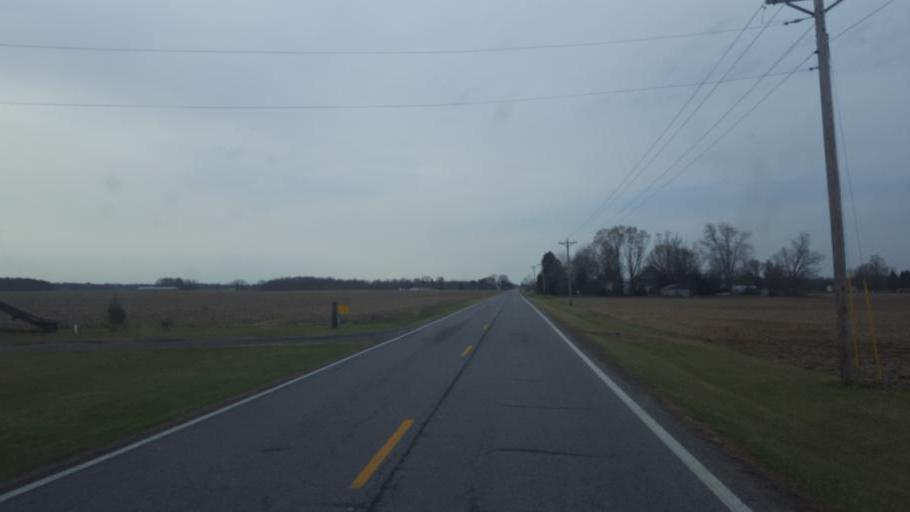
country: US
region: Ohio
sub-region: Morrow County
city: Cardington
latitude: 40.5911
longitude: -82.9624
